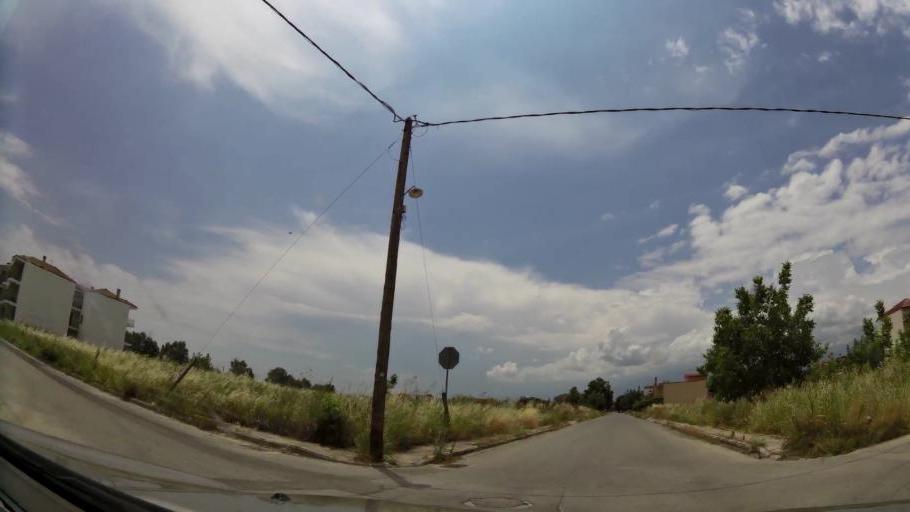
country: GR
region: Central Macedonia
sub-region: Nomos Pierias
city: Katerini
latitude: 40.2652
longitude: 22.5239
